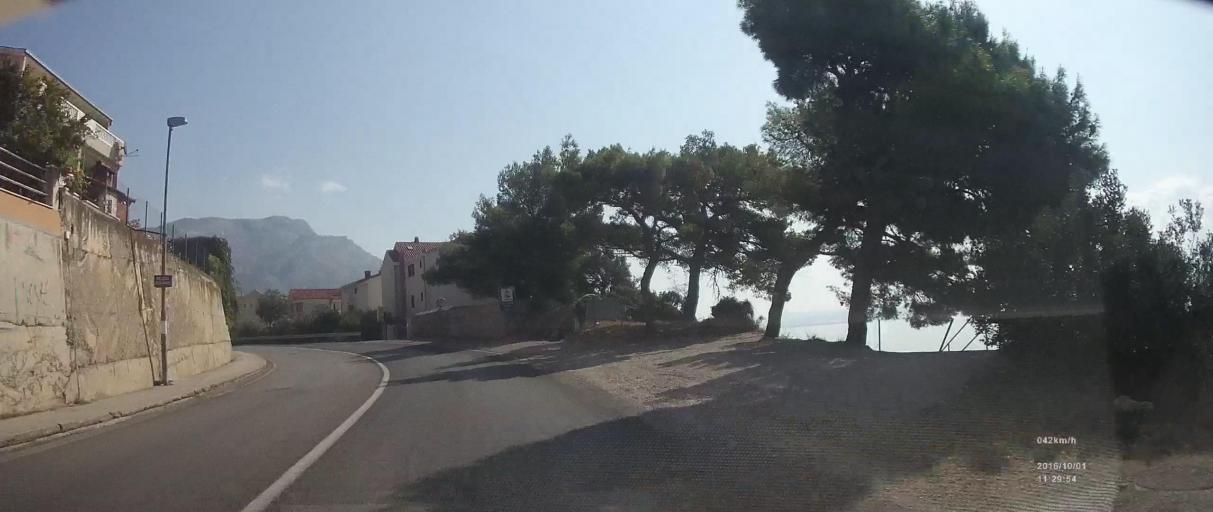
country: HR
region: Splitsko-Dalmatinska
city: Duce
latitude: 43.4398
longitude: 16.6710
